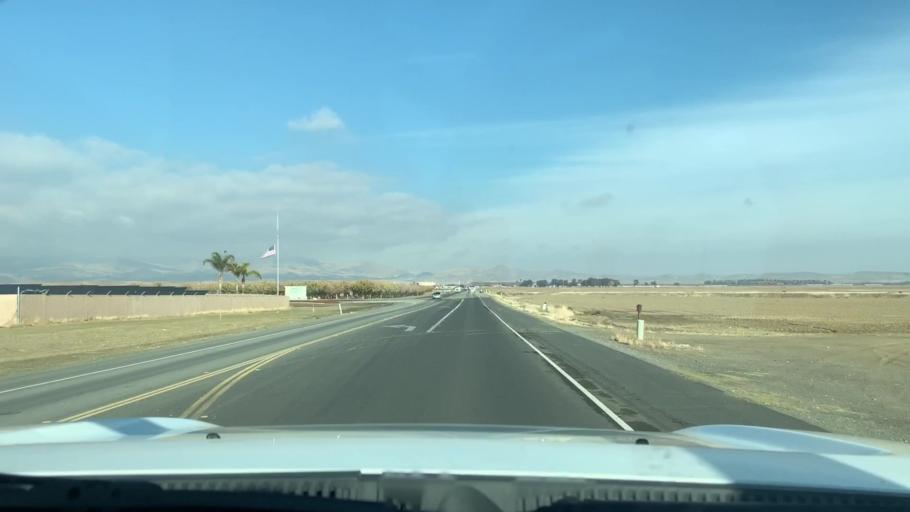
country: US
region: California
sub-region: Fresno County
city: Coalinga
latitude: 36.1652
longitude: -120.3546
